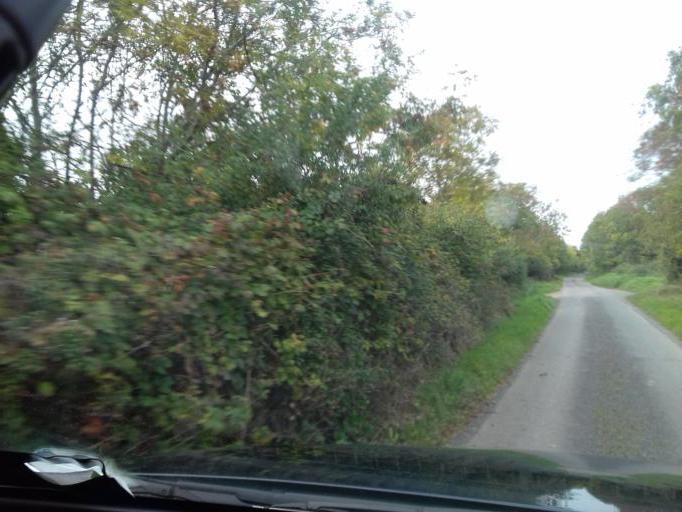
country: IE
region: Leinster
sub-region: Dublin City
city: Finglas
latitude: 53.4182
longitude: -6.3009
